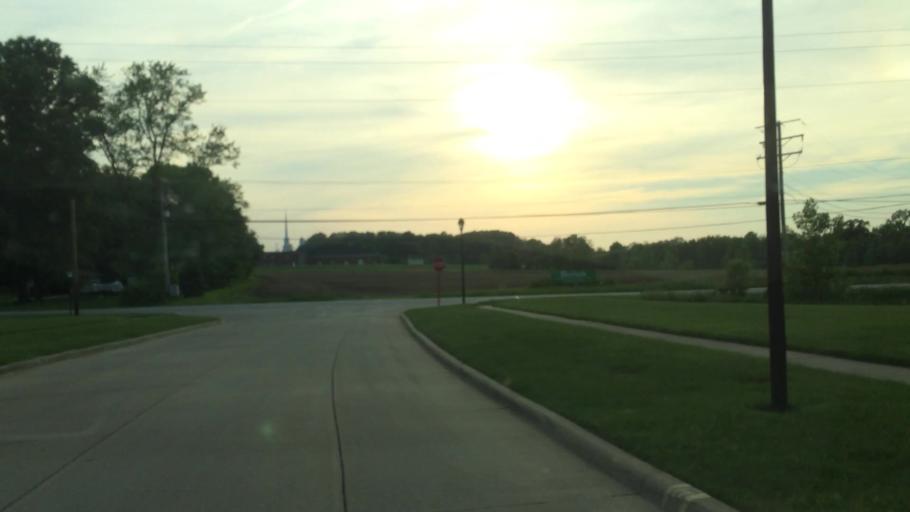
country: US
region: Ohio
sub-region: Medina County
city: Wadsworth
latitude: 41.0663
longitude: -81.7271
